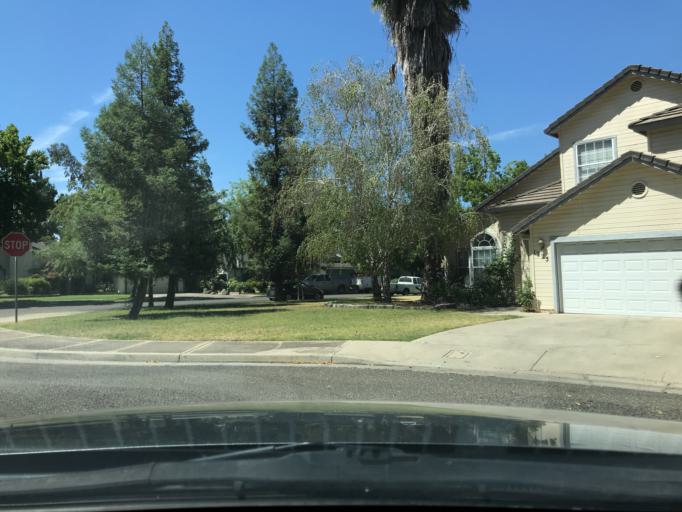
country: US
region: California
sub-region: Merced County
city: Merced
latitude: 37.3256
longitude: -120.4914
